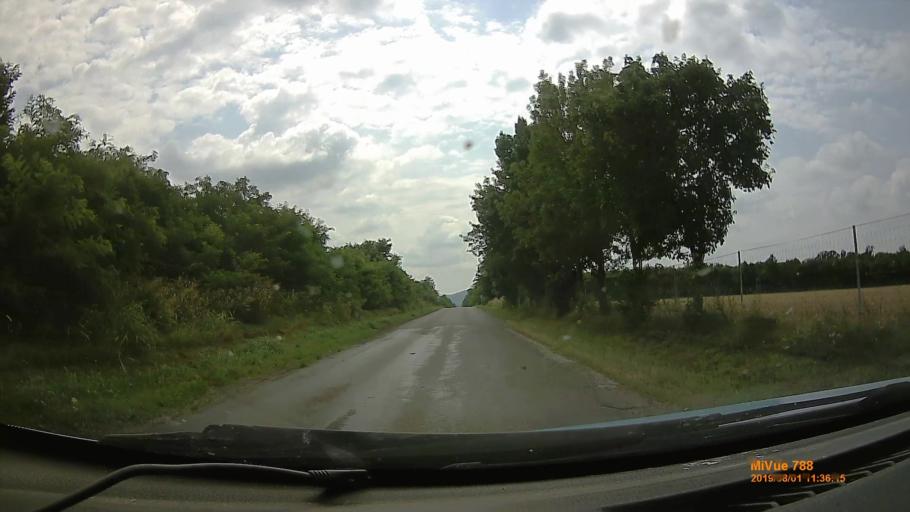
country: HU
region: Baranya
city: Villany
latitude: 45.9191
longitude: 18.3740
